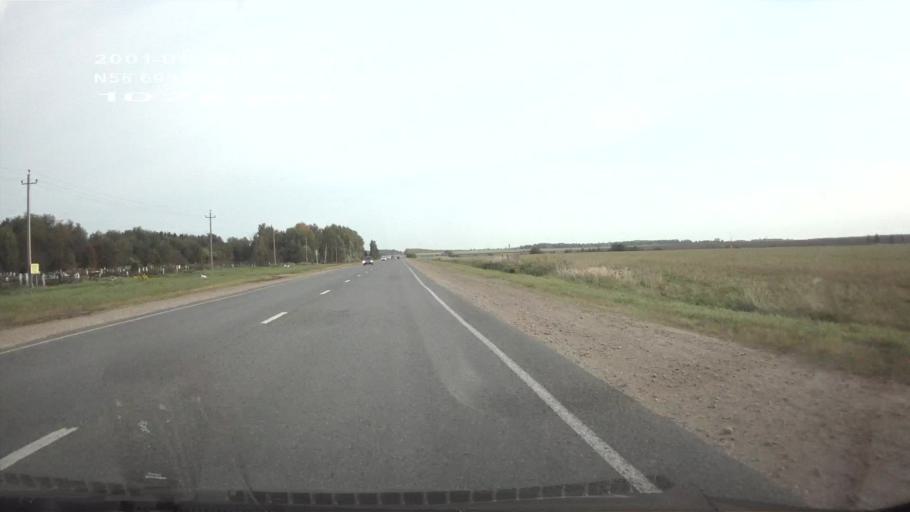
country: RU
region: Mariy-El
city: Yoshkar-Ola
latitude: 56.6982
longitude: 48.0638
